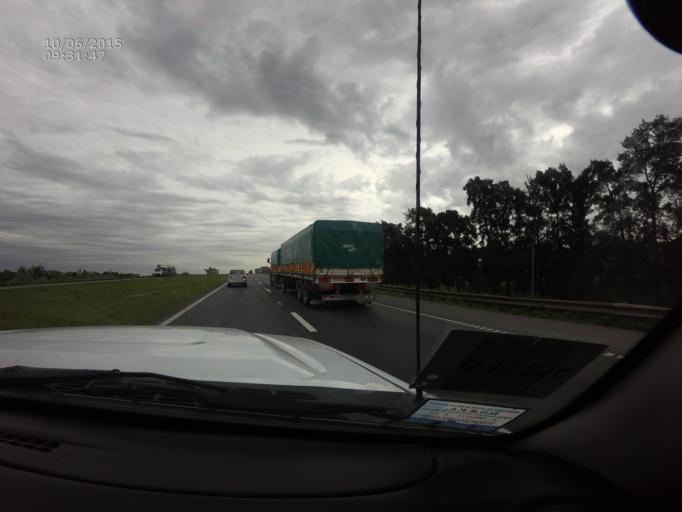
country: AR
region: Buenos Aires
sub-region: Partido de Zarate
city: Zarate
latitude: -34.1319
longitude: -59.0678
